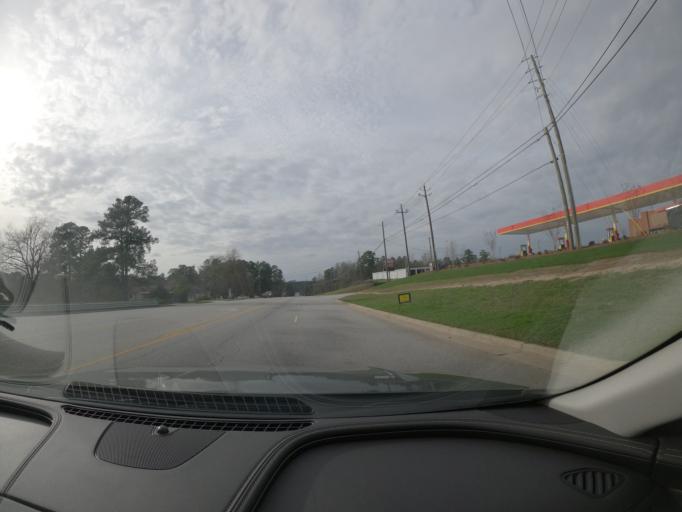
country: US
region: Georgia
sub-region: Columbia County
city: Evans
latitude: 33.4746
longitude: -82.1305
